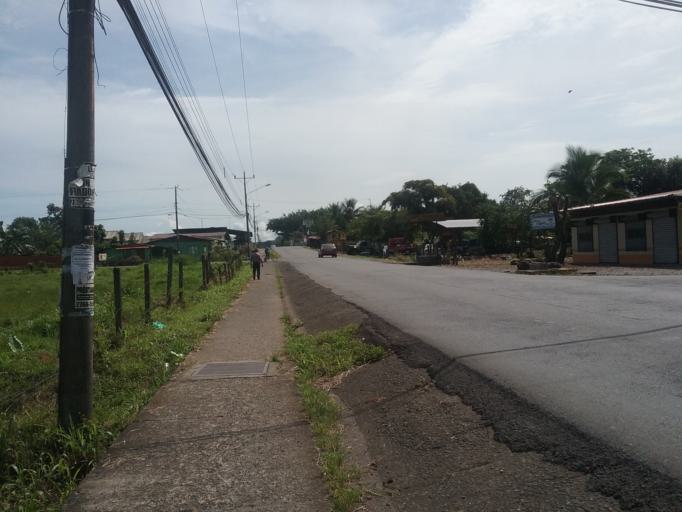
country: CR
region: Limon
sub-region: Canton de Pococi
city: Guapiles
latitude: 10.3204
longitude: -83.9042
